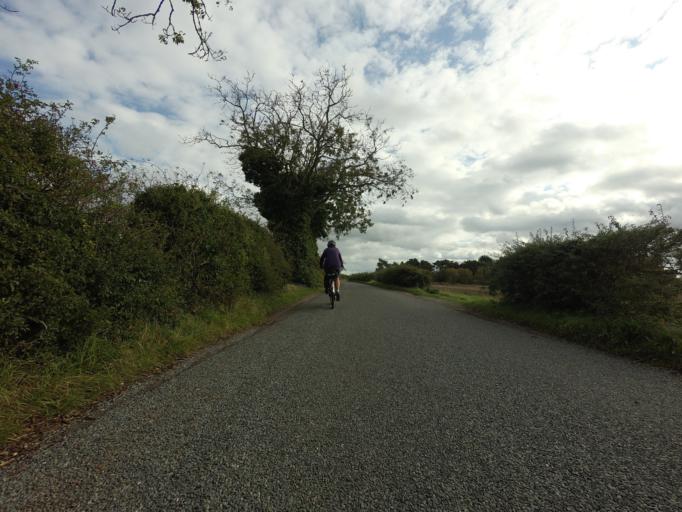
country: GB
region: England
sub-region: Norfolk
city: Dersingham
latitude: 52.8565
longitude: 0.5161
